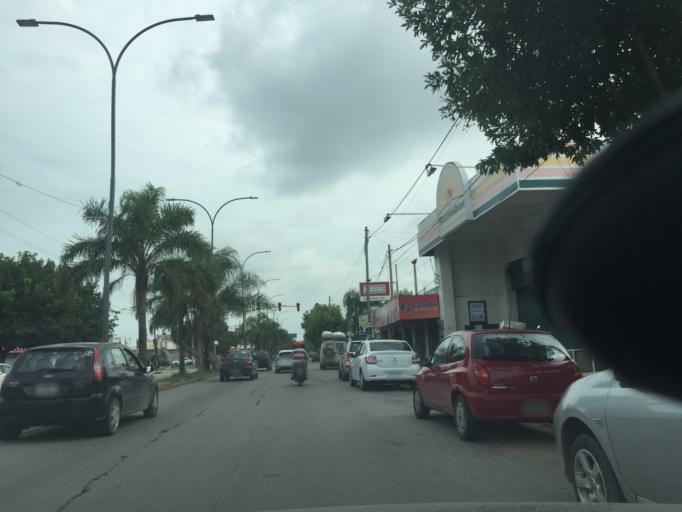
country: AR
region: Cordoba
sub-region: Departamento de Capital
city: Cordoba
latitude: -31.4488
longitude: -64.1995
